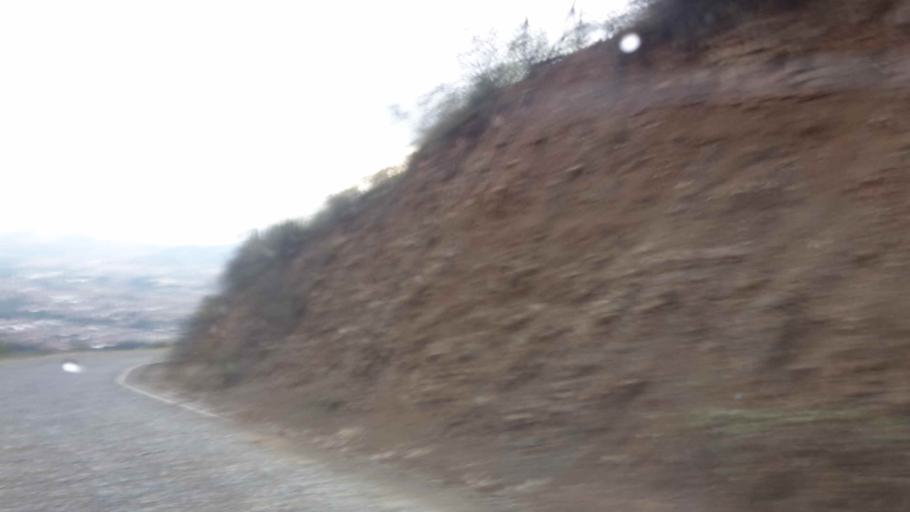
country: BO
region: Cochabamba
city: Cochabamba
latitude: -17.3694
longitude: -66.0620
